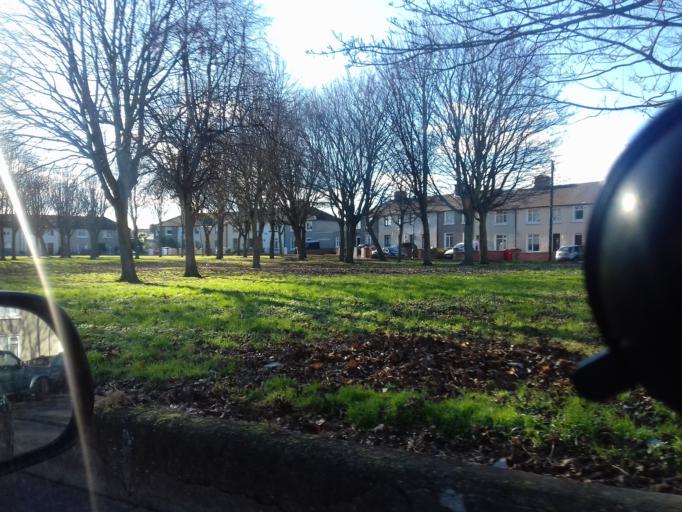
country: IE
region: Leinster
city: Marino
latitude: 53.3675
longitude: -6.2360
